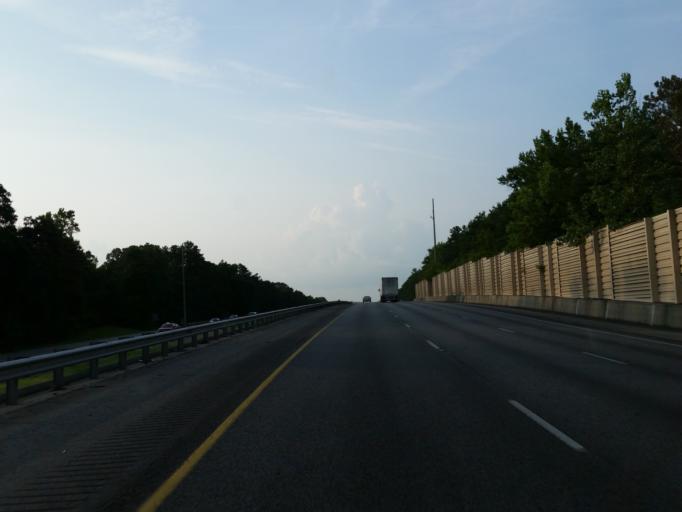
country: US
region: Georgia
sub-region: Bibb County
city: West Point
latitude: 32.7884
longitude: -83.7195
